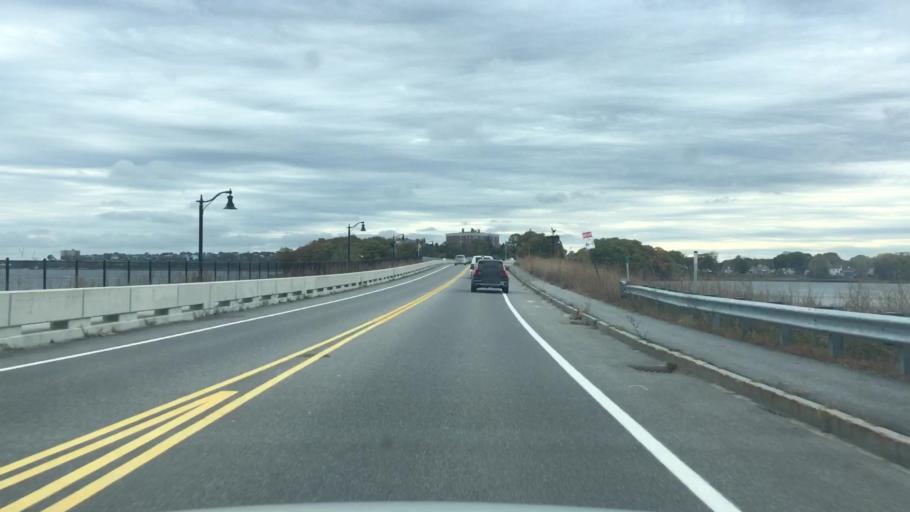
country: US
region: Maine
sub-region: Cumberland County
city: Portland
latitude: 43.6942
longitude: -70.2435
